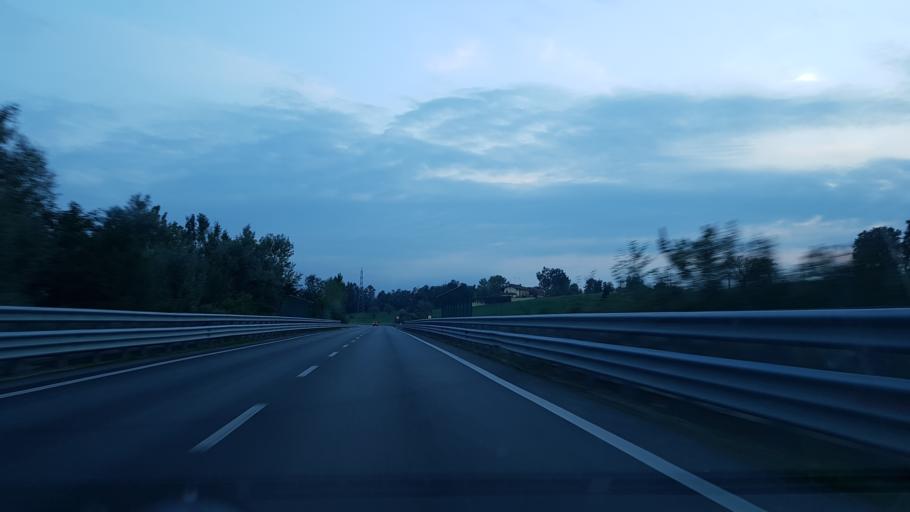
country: IT
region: Piedmont
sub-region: Provincia di Cuneo
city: Mondovi
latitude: 44.4030
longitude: 7.8003
